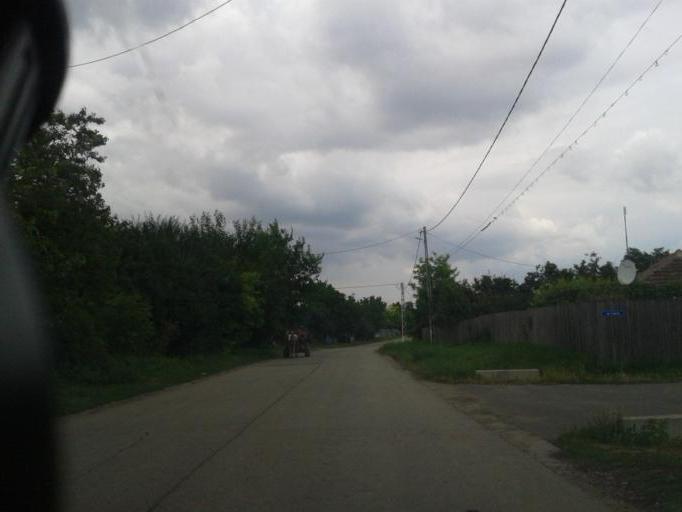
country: RO
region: Calarasi
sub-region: Comuna Fundulea
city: Fundulea
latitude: 44.5034
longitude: 26.4957
